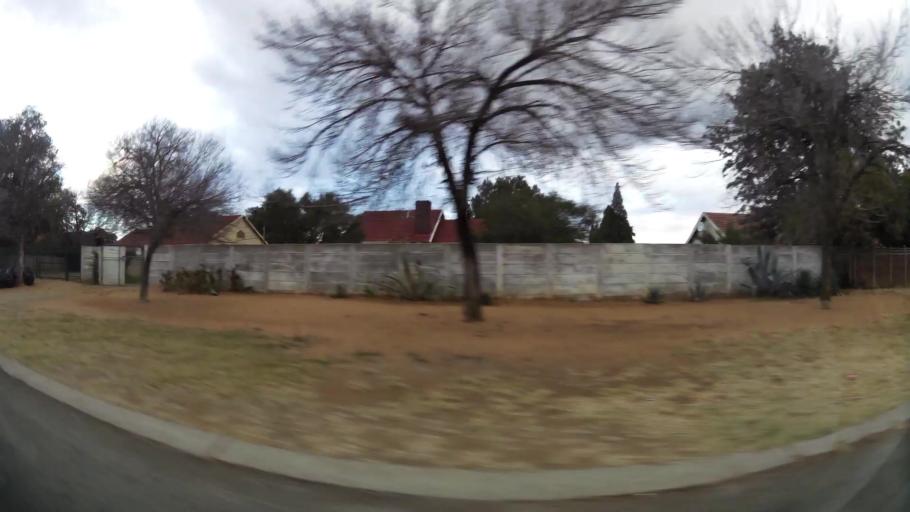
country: ZA
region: Orange Free State
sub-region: Lejweleputswa District Municipality
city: Welkom
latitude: -27.9616
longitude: 26.7226
